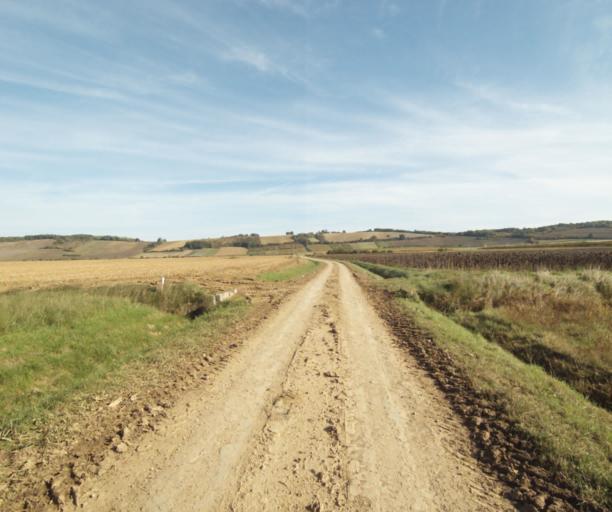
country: FR
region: Midi-Pyrenees
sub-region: Departement du Tarn-et-Garonne
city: Orgueil
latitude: 43.9163
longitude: 1.4302
